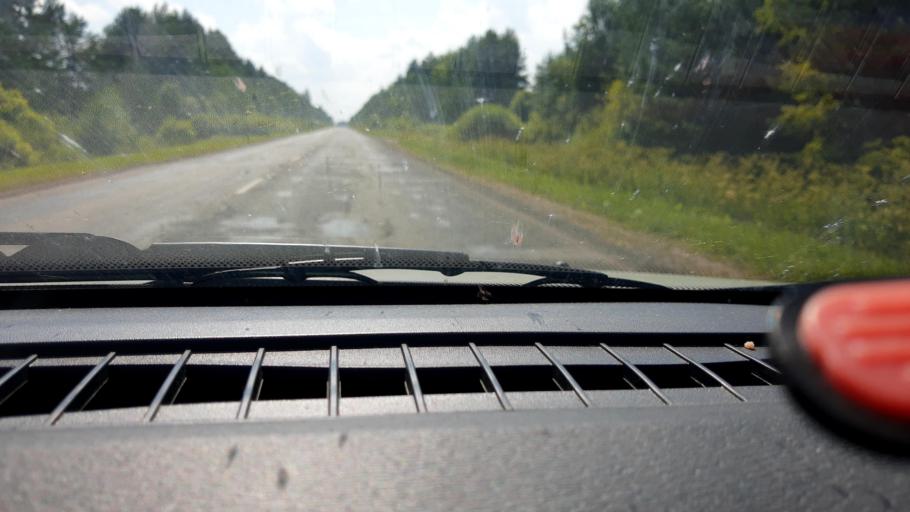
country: RU
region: Nizjnij Novgorod
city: Tonkino
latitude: 57.3607
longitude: 46.3320
